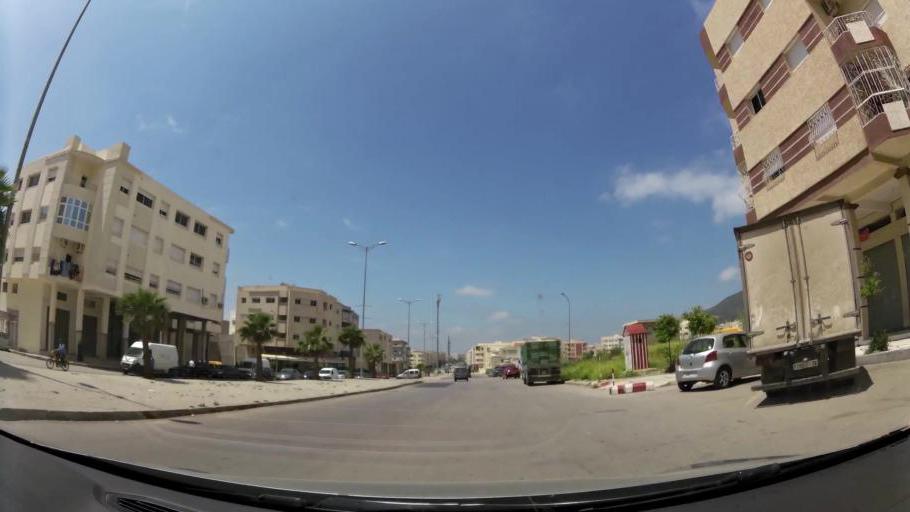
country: MA
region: Fes-Boulemane
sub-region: Fes
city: Fes
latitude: 34.0594
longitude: -5.0258
